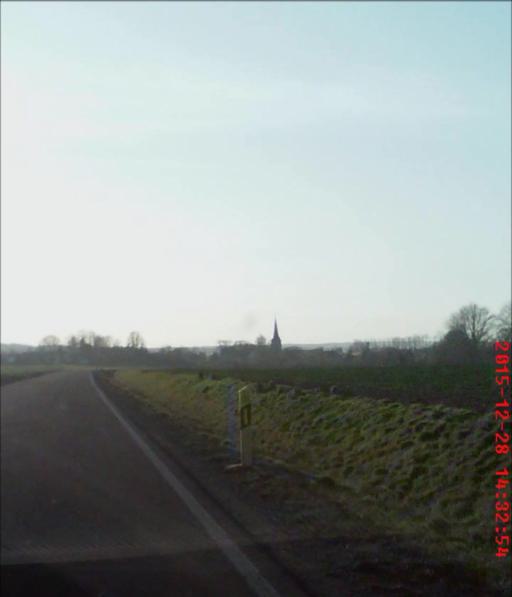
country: DE
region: Thuringia
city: Wohlsborn
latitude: 51.0388
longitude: 11.3519
